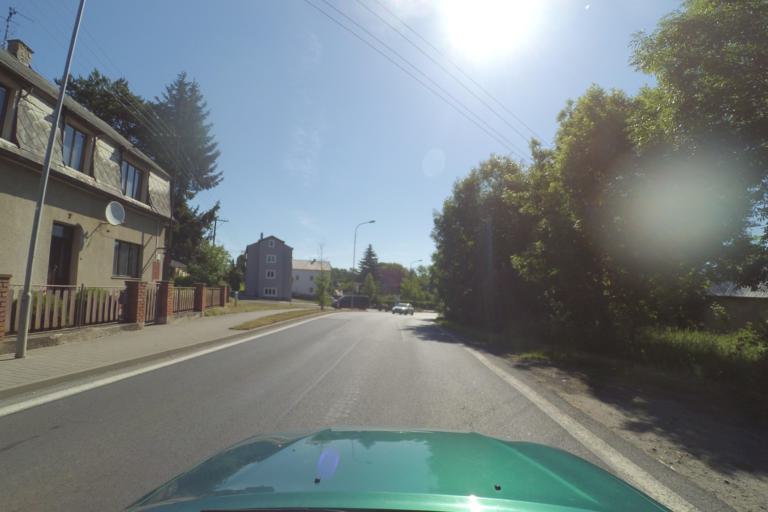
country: CZ
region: Karlovarsky
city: Nova Role
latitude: 50.2376
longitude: 12.8065
